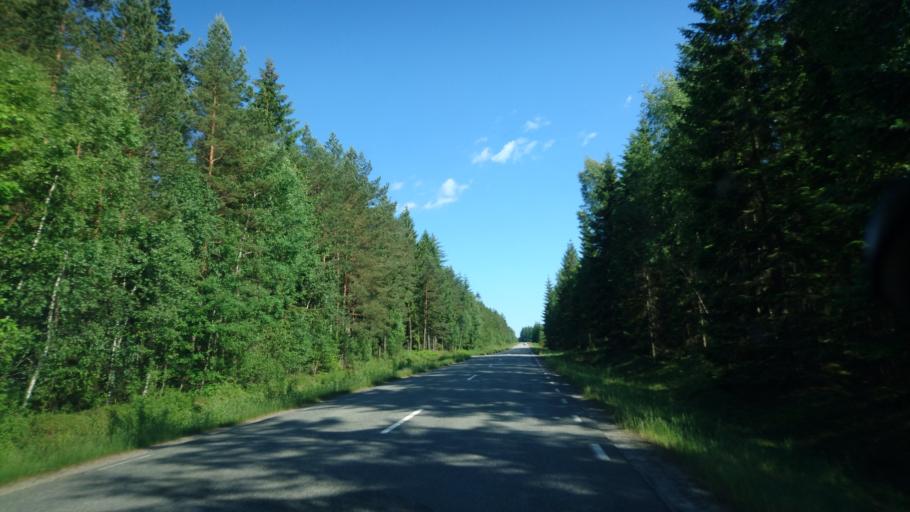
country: SE
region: Skane
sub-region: Osby Kommun
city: Lonsboda
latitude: 56.4376
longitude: 14.2512
